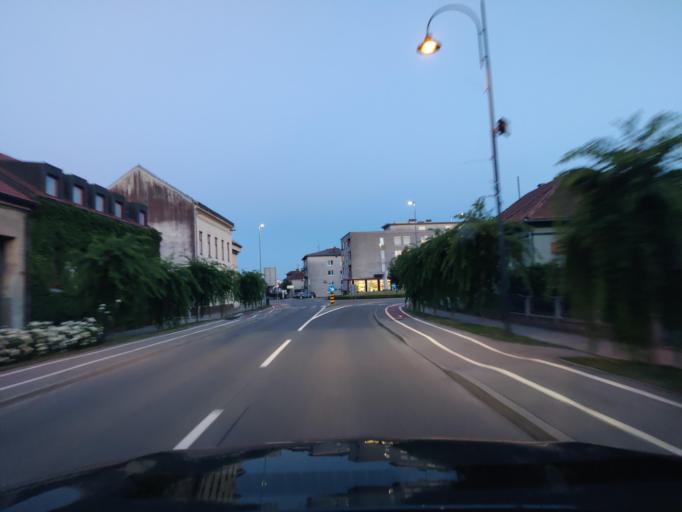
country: SI
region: Lendava-Lendva
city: Lendava
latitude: 46.5629
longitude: 16.4533
